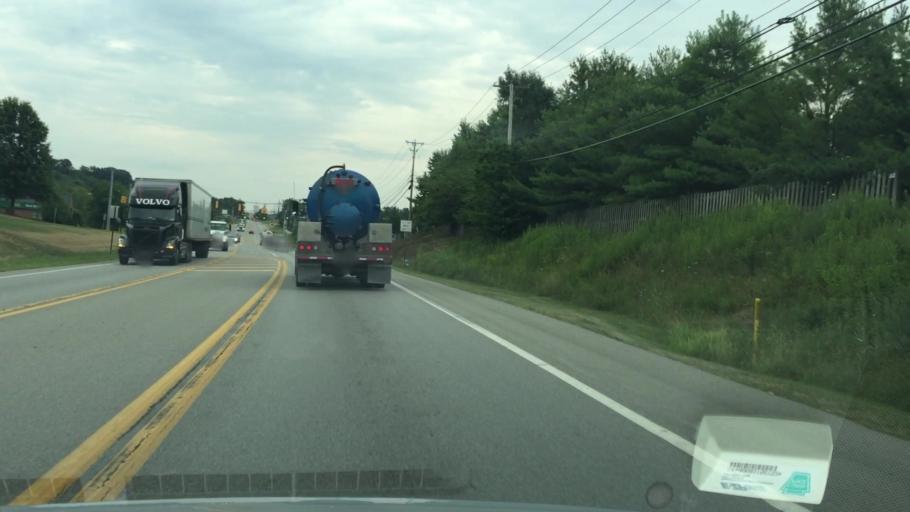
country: US
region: Pennsylvania
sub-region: Butler County
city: Seven Fields
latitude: 40.6863
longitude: -80.0603
